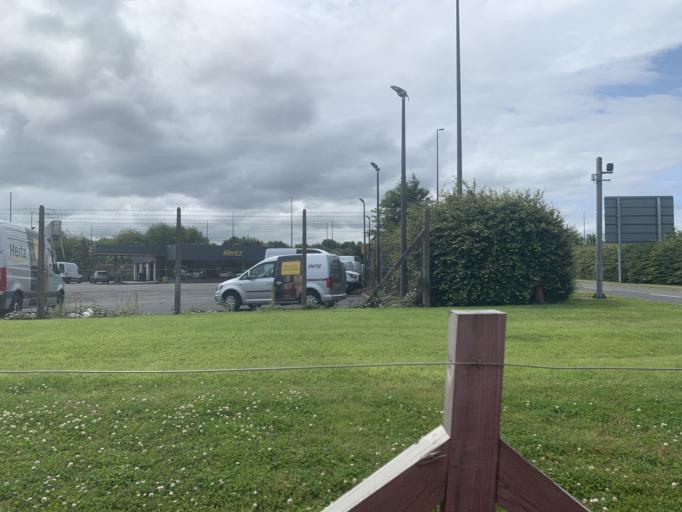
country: GB
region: Scotland
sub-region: Renfrewshire
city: Inchinnan
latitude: 55.8627
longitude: -4.4361
